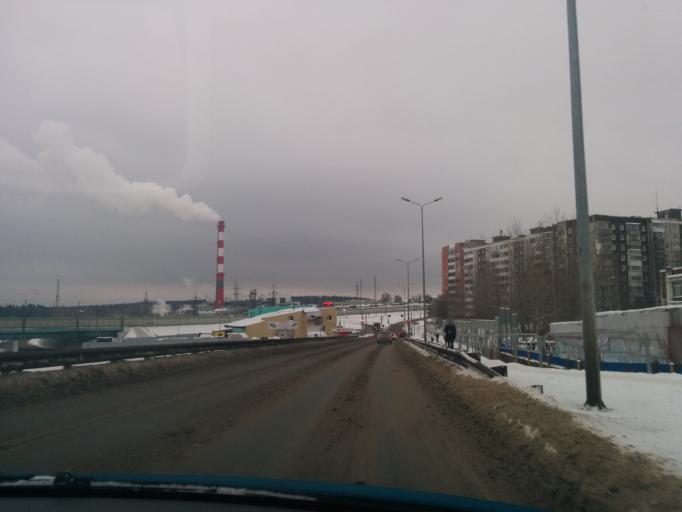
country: RU
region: Perm
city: Perm
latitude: 58.0039
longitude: 56.3134
